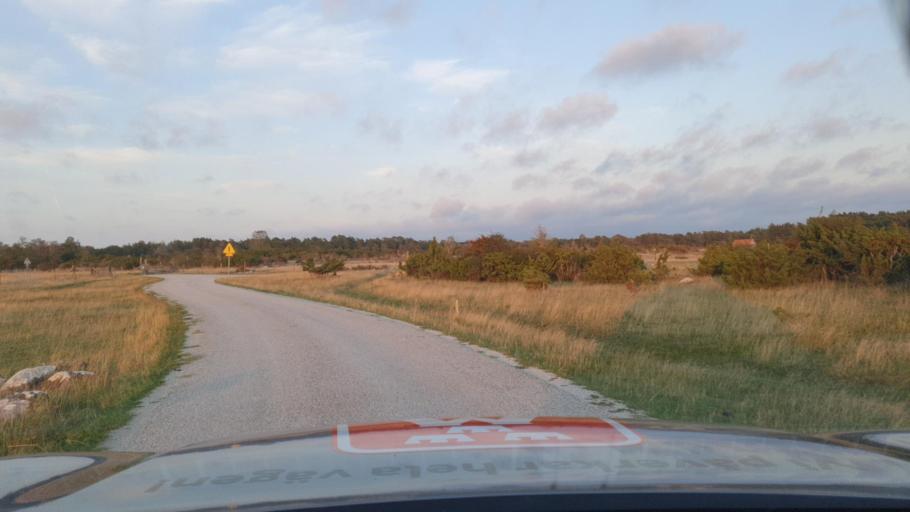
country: SE
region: Gotland
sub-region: Gotland
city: Klintehamn
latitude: 57.2568
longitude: 18.1129
